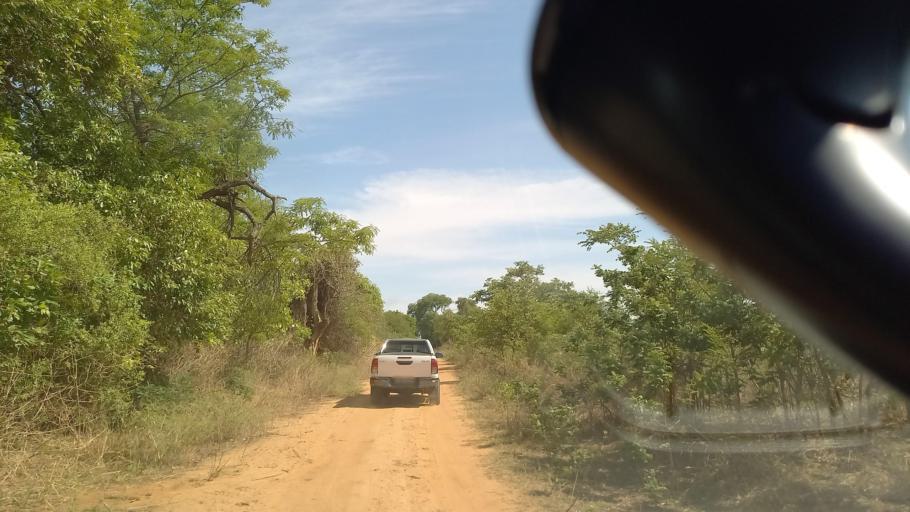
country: ZM
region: Southern
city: Mazabuka
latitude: -16.0378
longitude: 27.6224
